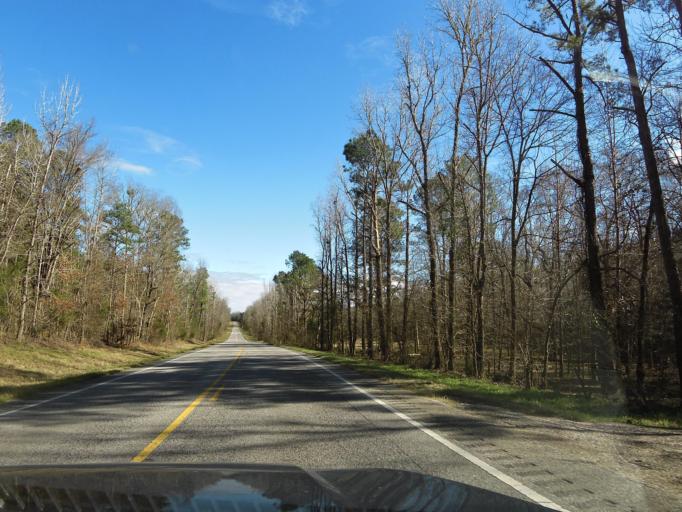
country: US
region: Alabama
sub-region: Barbour County
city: Clayton
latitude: 32.0367
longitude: -85.4068
